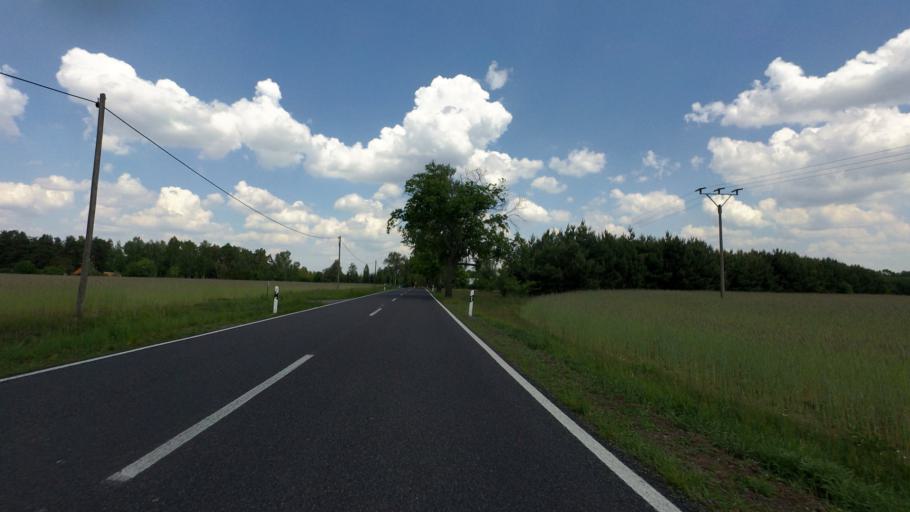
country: DE
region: Brandenburg
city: Lieberose
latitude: 51.9786
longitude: 14.2161
